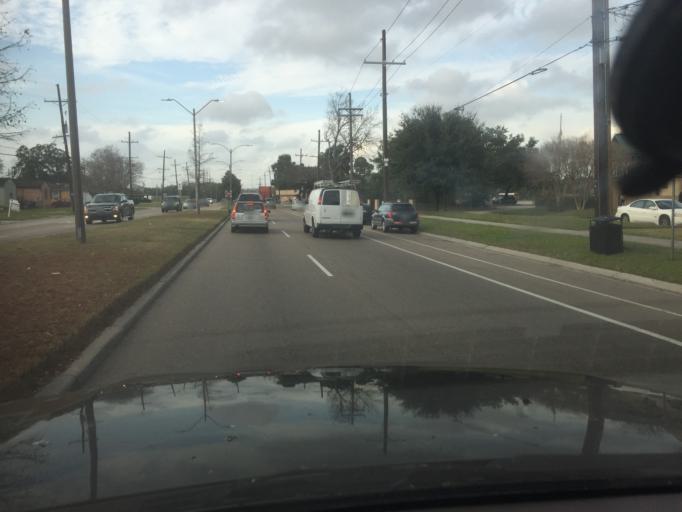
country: US
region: Louisiana
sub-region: Orleans Parish
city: New Orleans
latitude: 29.9890
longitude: -90.0749
